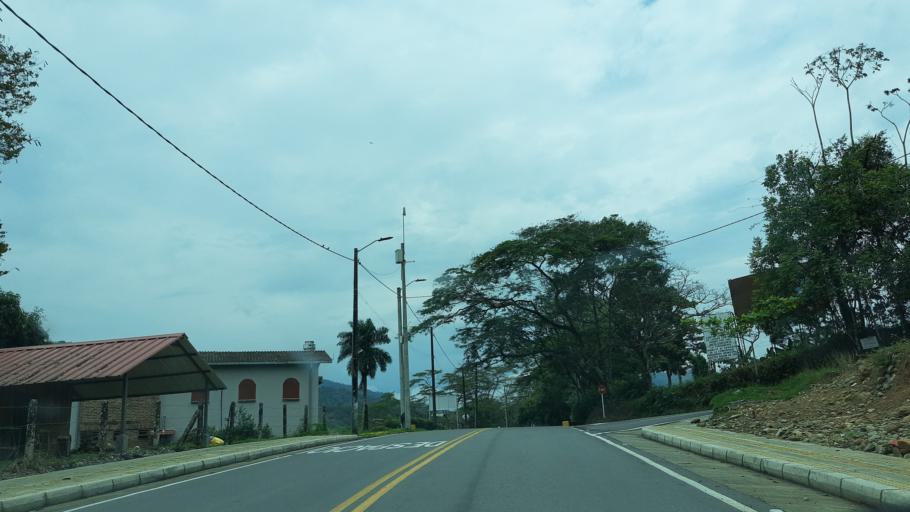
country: CO
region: Casanare
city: Sabanalarga
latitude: 4.8183
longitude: -73.0699
